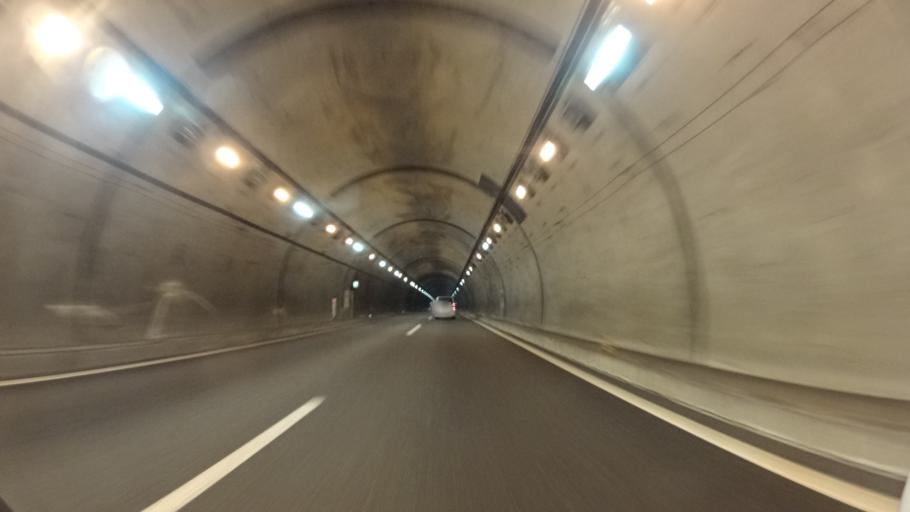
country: JP
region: Ehime
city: Saijo
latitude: 33.8862
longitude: 133.1578
